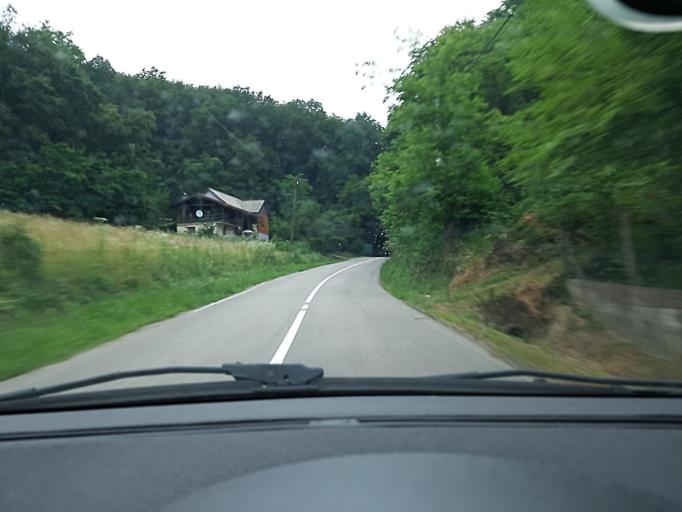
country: HR
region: Zagrebacka
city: Jakovlje
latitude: 45.9798
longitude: 15.8363
